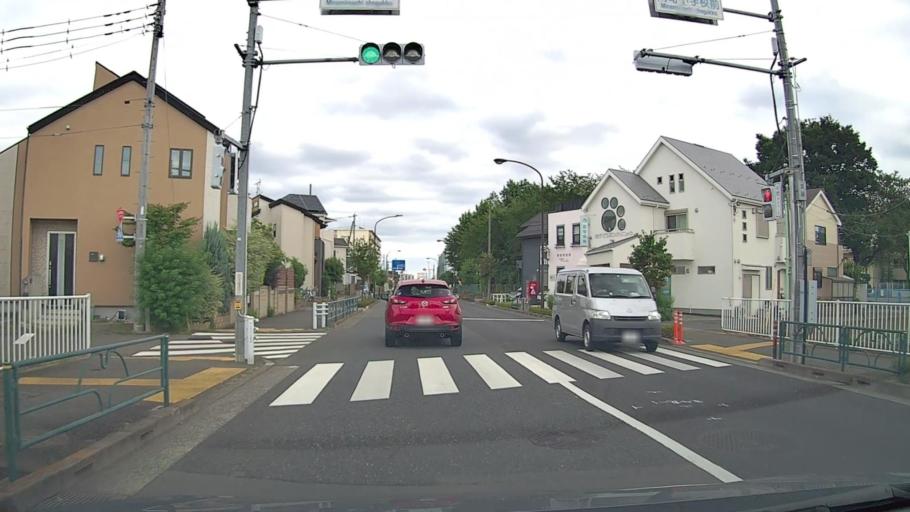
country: JP
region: Tokyo
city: Tanashicho
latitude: 35.7422
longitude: 139.5237
